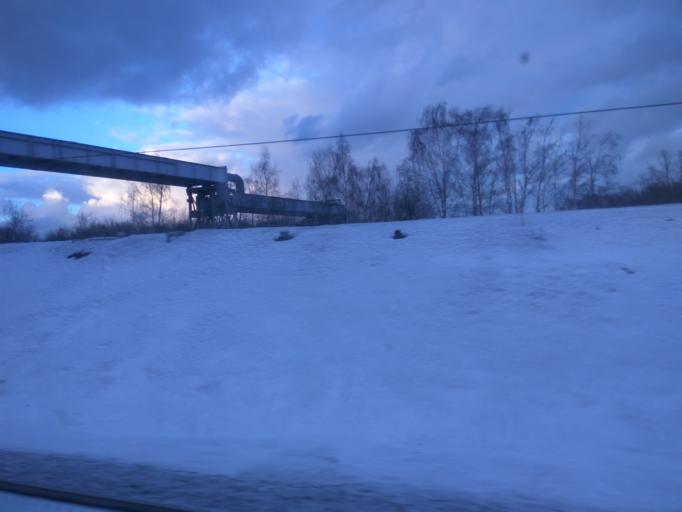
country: RU
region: Moscow
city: Tsaritsyno
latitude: 55.6182
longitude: 37.6329
